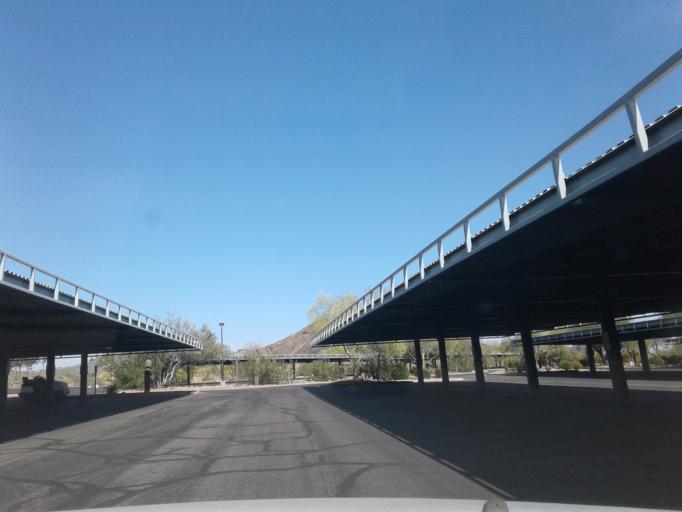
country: US
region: Arizona
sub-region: Maricopa County
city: Fountain Hills
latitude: 33.5870
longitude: -111.7937
